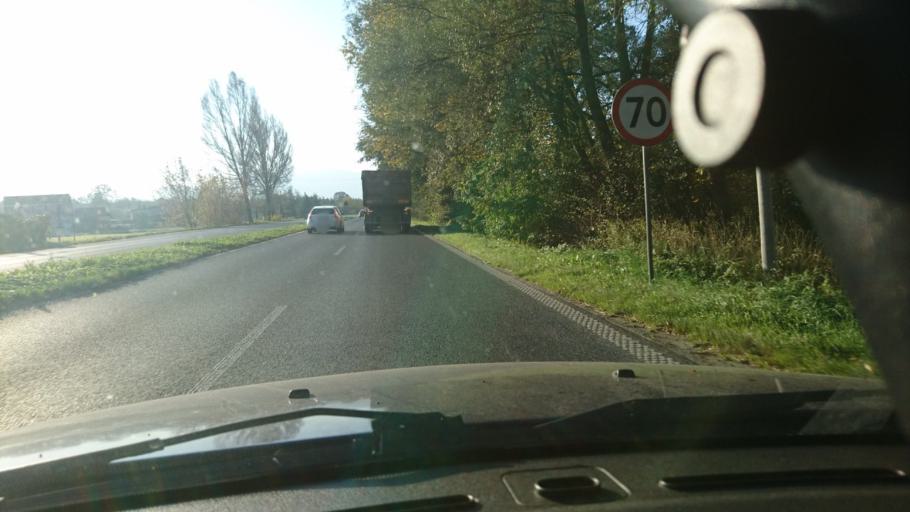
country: PL
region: Silesian Voivodeship
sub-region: Powiat cieszynski
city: Gorki Wielkie
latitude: 49.7812
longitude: 18.8068
